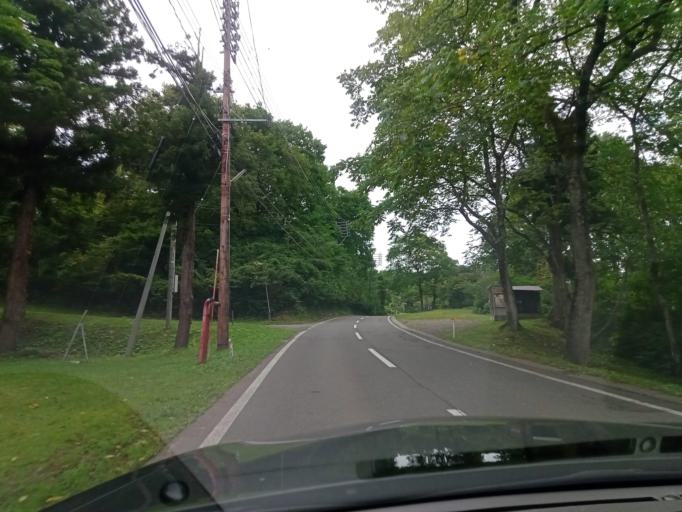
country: JP
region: Niigata
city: Arai
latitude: 36.8817
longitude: 138.1808
